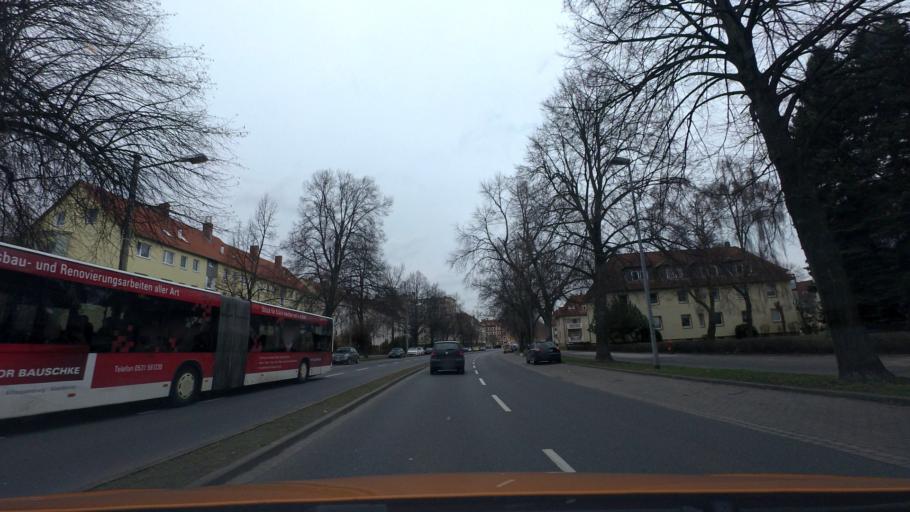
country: DE
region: Lower Saxony
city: Braunschweig
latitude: 52.2675
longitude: 10.5001
